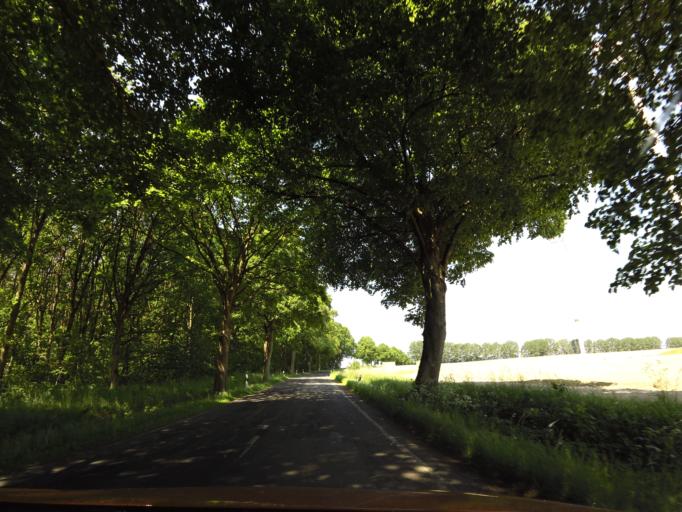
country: DE
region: Mecklenburg-Vorpommern
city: Neuburg
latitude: 53.4120
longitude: 11.8914
